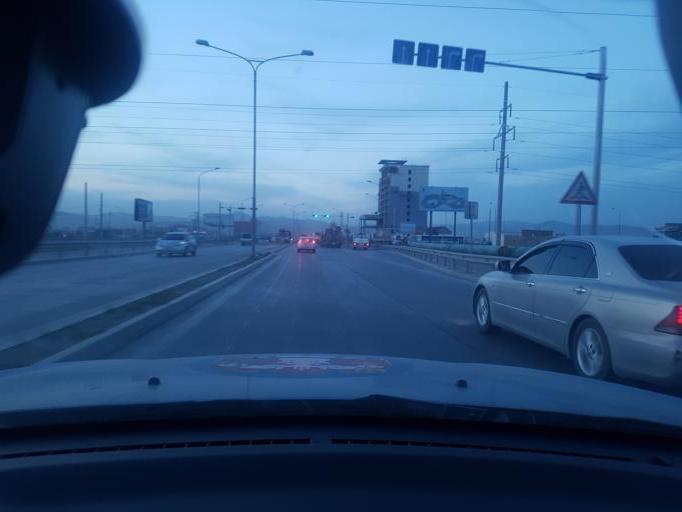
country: MN
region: Ulaanbaatar
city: Ulaanbaatar
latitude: 47.8894
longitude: 106.7853
